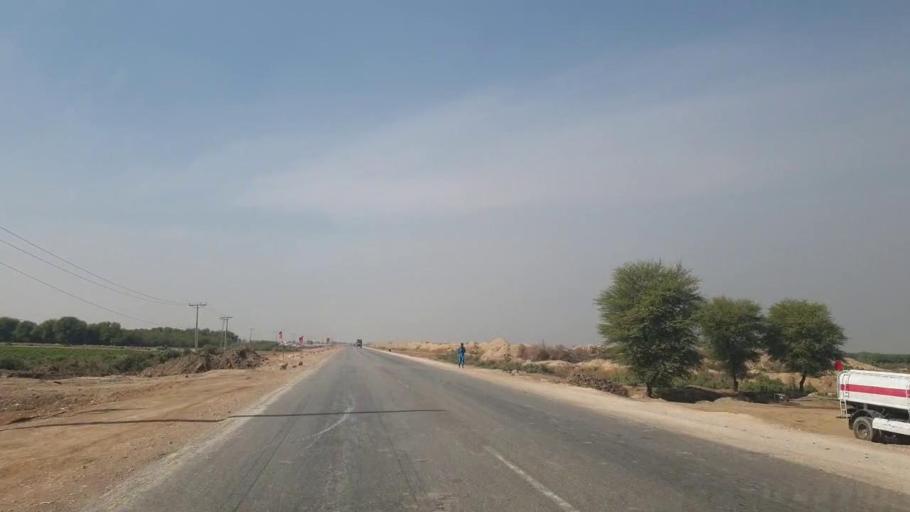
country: PK
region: Sindh
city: Sann
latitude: 26.0030
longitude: 68.1590
